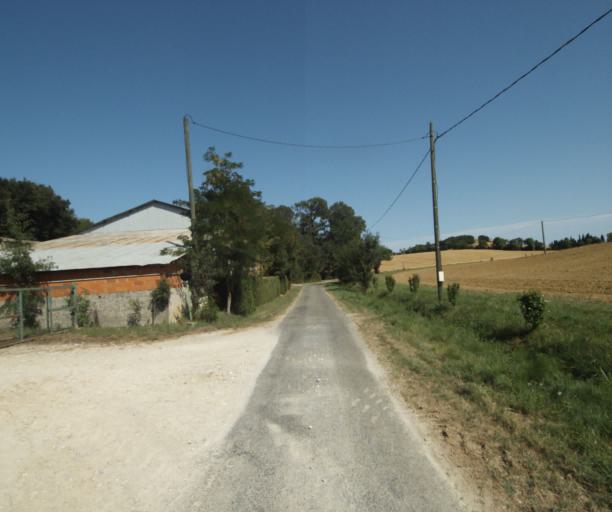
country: FR
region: Midi-Pyrenees
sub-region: Departement de la Haute-Garonne
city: Saint-Felix-Lauragais
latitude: 43.4367
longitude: 1.8437
